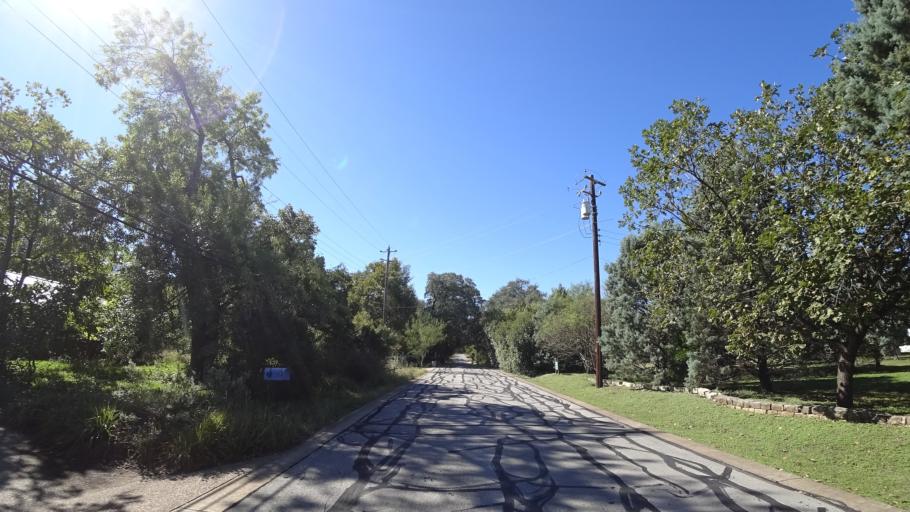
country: US
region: Texas
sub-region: Travis County
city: Rollingwood
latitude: 30.2277
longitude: -97.8098
